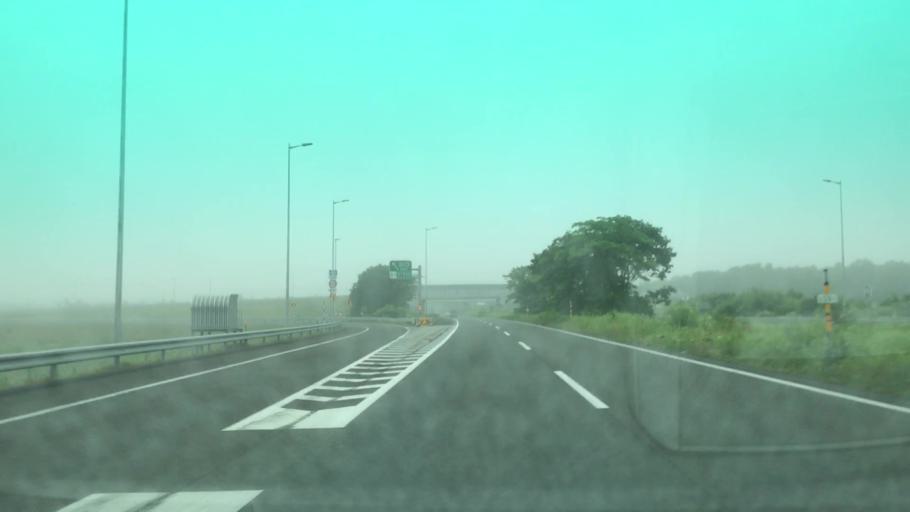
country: JP
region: Hokkaido
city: Chitose
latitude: 42.7787
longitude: 141.6275
